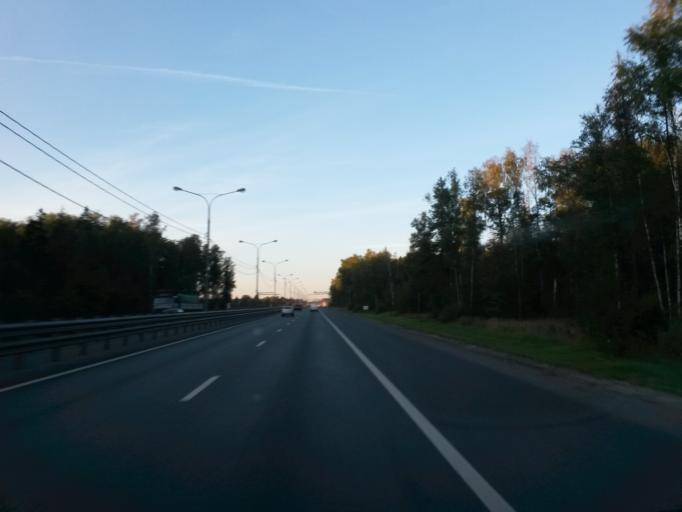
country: RU
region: Moskovskaya
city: Pushkino
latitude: 56.0304
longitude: 37.8870
